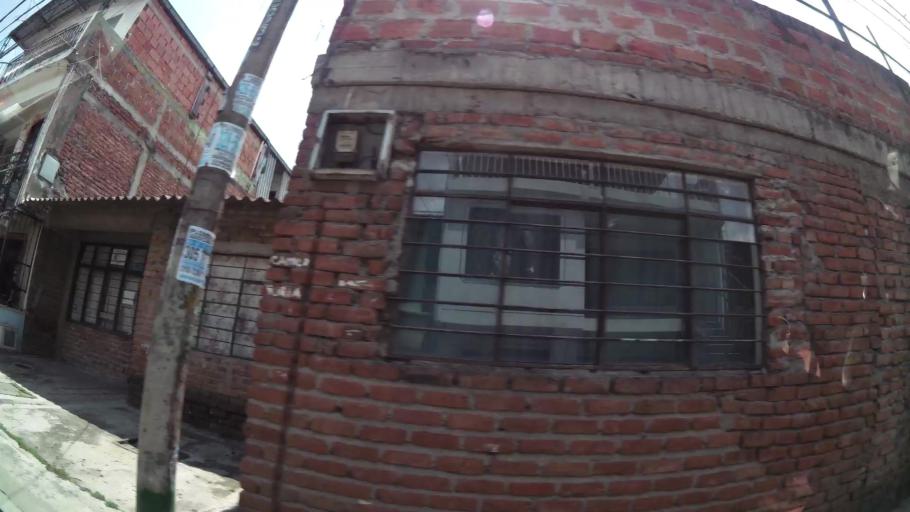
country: CO
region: Valle del Cauca
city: Cali
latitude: 3.4656
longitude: -76.4819
